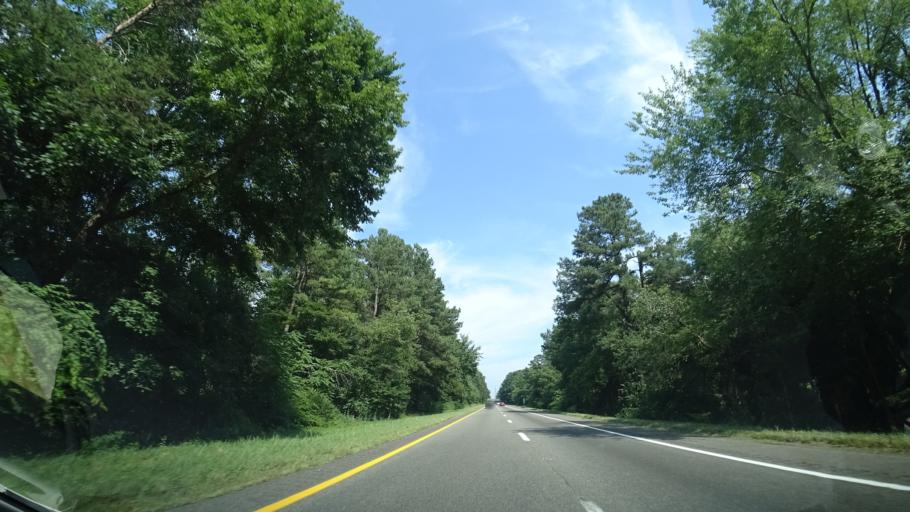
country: US
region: Virginia
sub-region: Goochland County
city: Goochland
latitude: 37.7045
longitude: -77.7632
